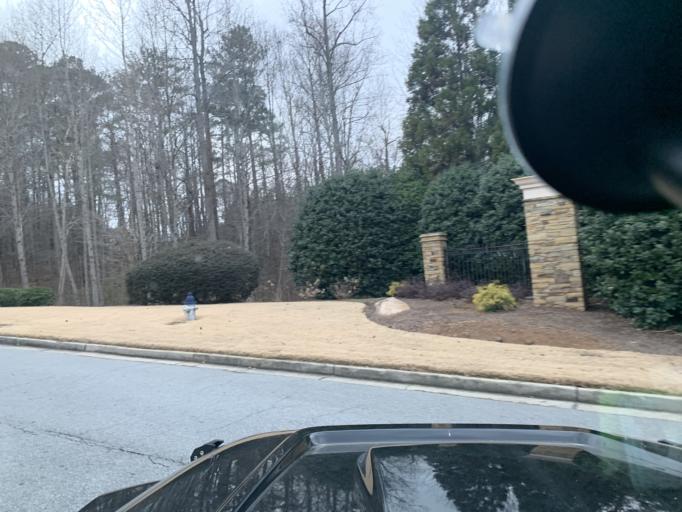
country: US
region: Georgia
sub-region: Cherokee County
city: Woodstock
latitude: 34.1008
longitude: -84.4661
